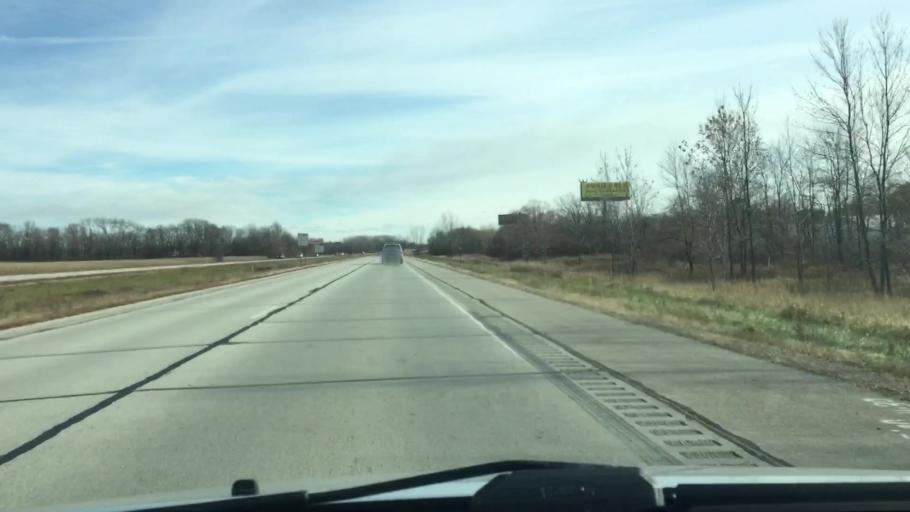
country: US
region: Wisconsin
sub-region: Brown County
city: Pulaski
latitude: 44.5905
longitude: -88.2041
